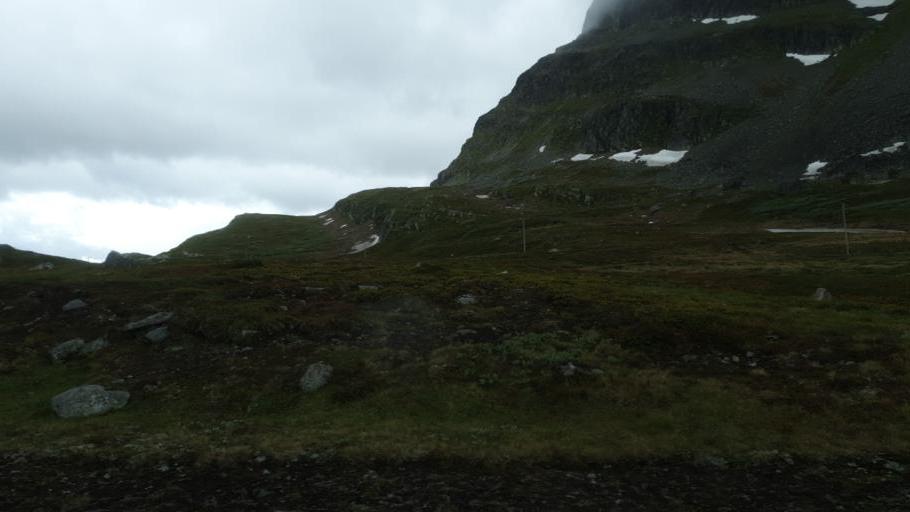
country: NO
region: Oppland
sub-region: Vestre Slidre
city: Slidre
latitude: 61.2993
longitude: 8.8120
